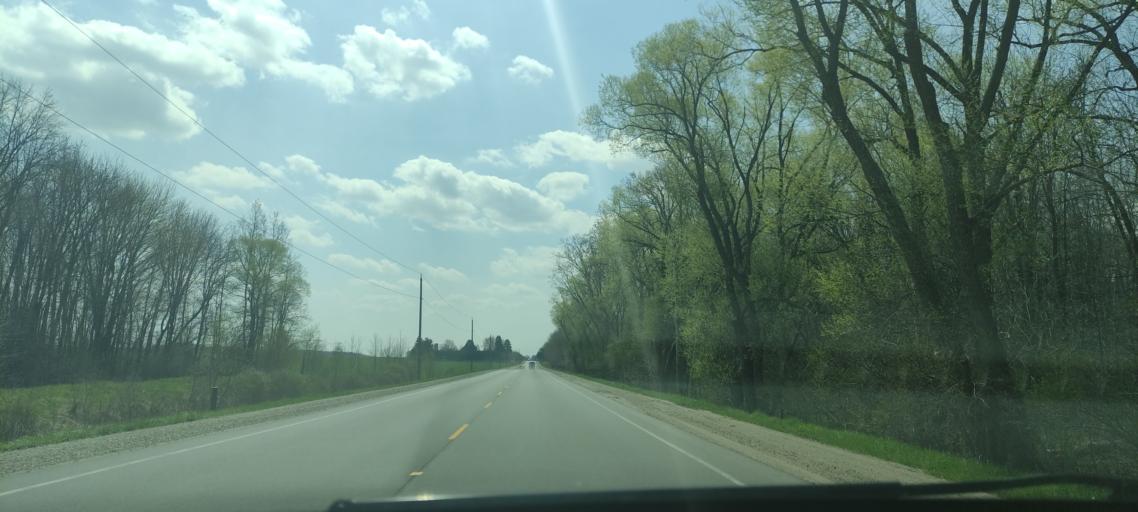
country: CA
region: Ontario
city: Stratford
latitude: 43.3414
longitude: -80.9988
